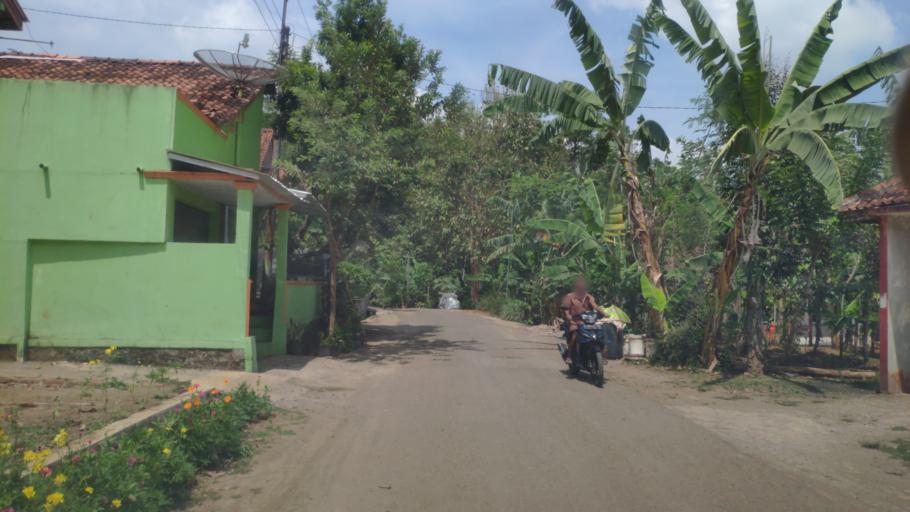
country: ID
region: Central Java
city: Wonosobo
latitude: -7.4230
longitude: 109.7867
